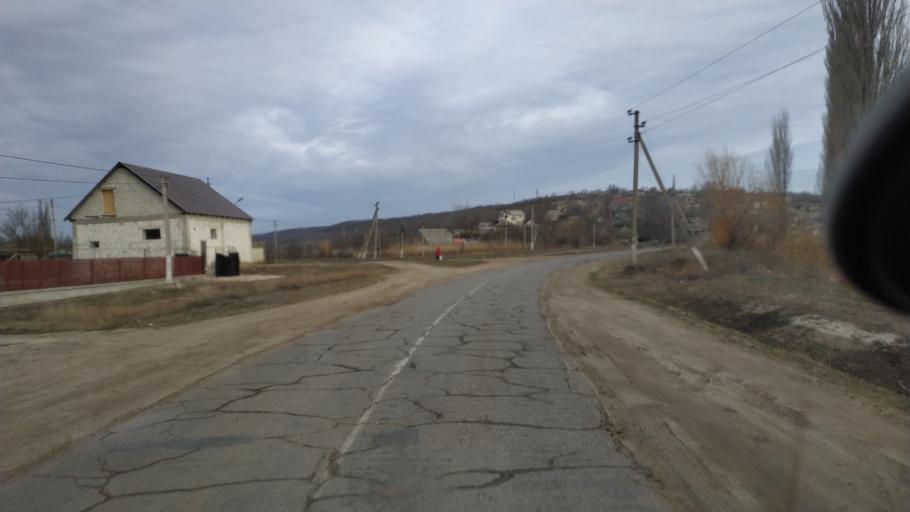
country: MD
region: Chisinau
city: Vadul lui Voda
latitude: 47.1381
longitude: 29.0610
